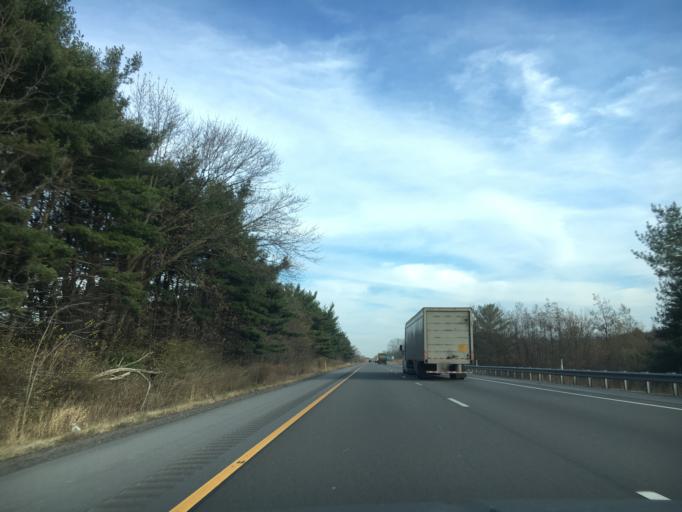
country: US
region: Pennsylvania
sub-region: Montour County
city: Danville
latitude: 40.9986
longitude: -76.6364
